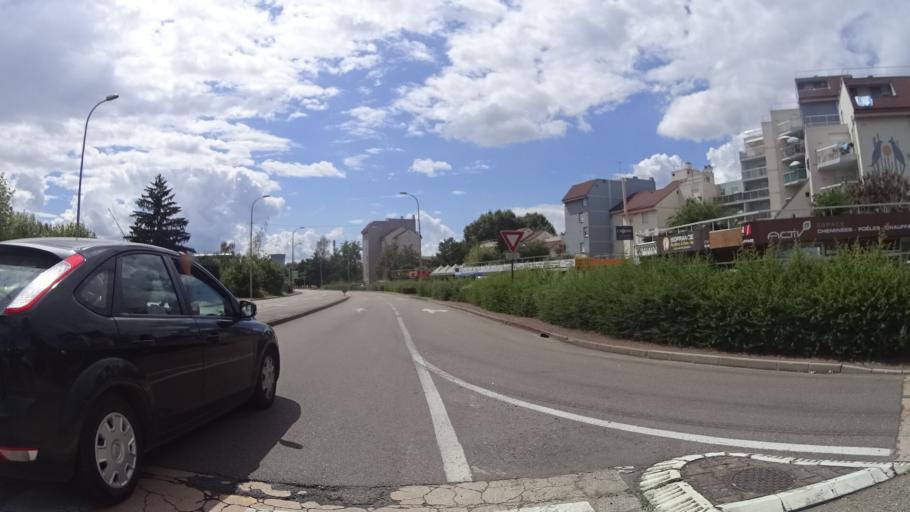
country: FR
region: Bourgogne
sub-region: Departement de Saone-et-Loire
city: Montceau-les-Mines
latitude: 46.6790
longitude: 4.3655
